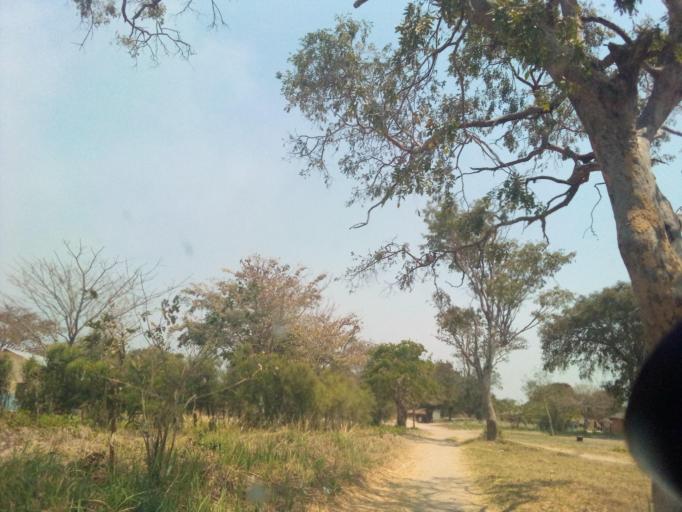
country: ZM
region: Copperbelt
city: Kataba
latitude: -12.2438
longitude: 30.3254
